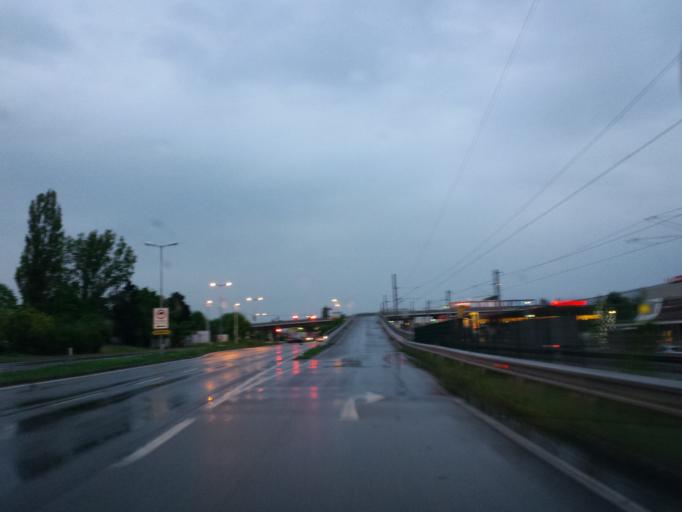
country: AT
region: Lower Austria
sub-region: Politischer Bezirk Modling
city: Vosendorf
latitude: 48.1121
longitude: 16.3154
